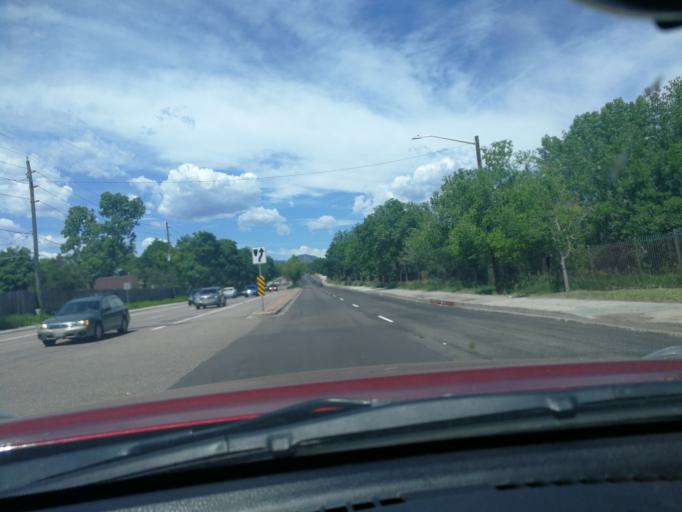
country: US
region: Colorado
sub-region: Jefferson County
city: Columbine
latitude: 39.6099
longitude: -105.0659
